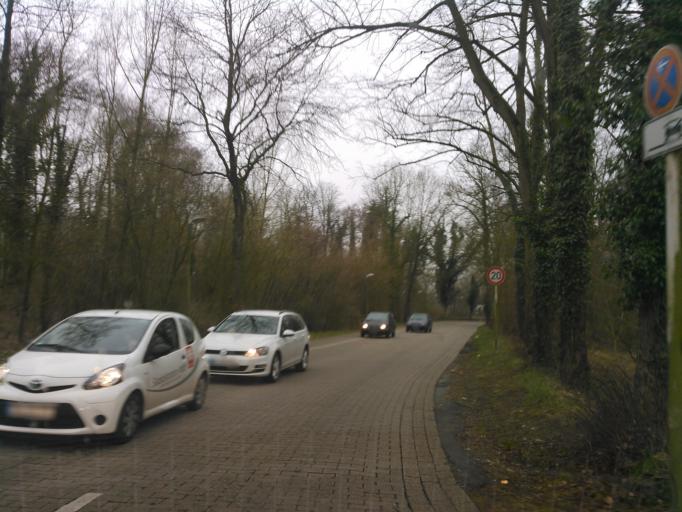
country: DE
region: North Rhine-Westphalia
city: Marl
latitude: 51.6544
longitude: 7.1364
